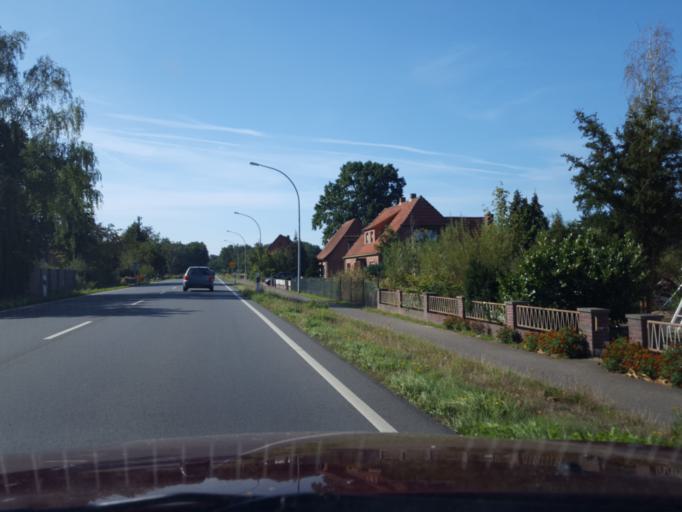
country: DE
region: Lower Saxony
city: Dorverden
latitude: 52.8352
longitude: 9.2141
